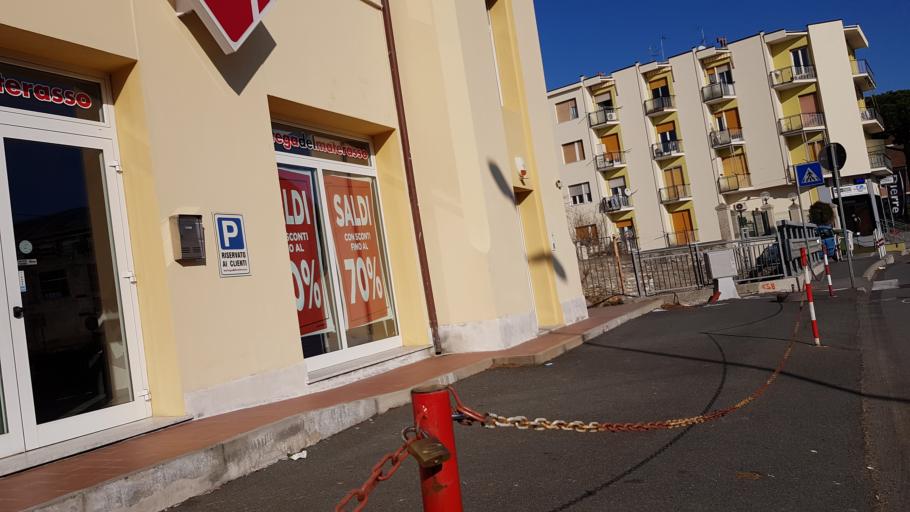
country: IT
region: Liguria
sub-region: Provincia di Savona
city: Savona
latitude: 44.2935
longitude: 8.4565
